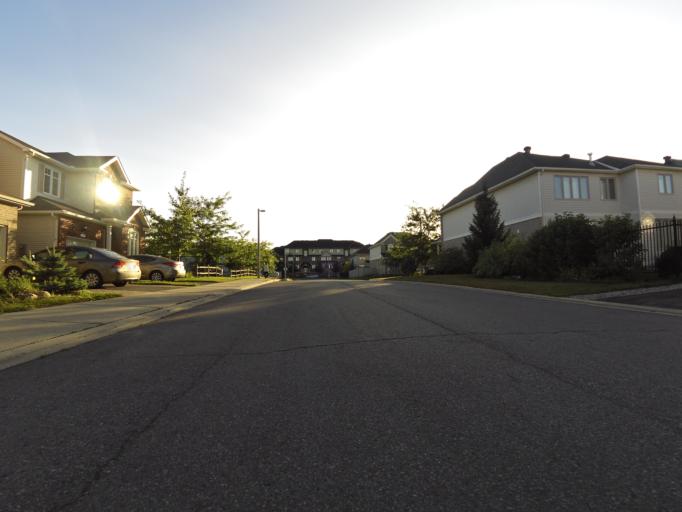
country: CA
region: Ontario
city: Bells Corners
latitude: 45.2756
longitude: -75.7422
